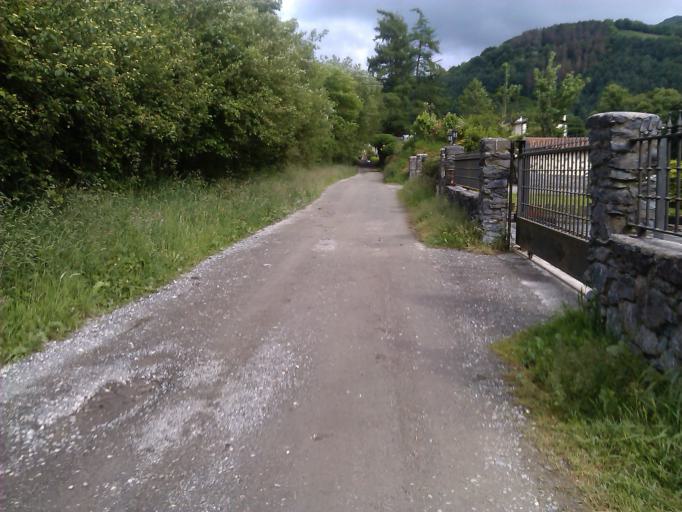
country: ES
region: Navarre
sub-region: Provincia de Navarra
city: Leitza
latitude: 43.0859
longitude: -1.9148
